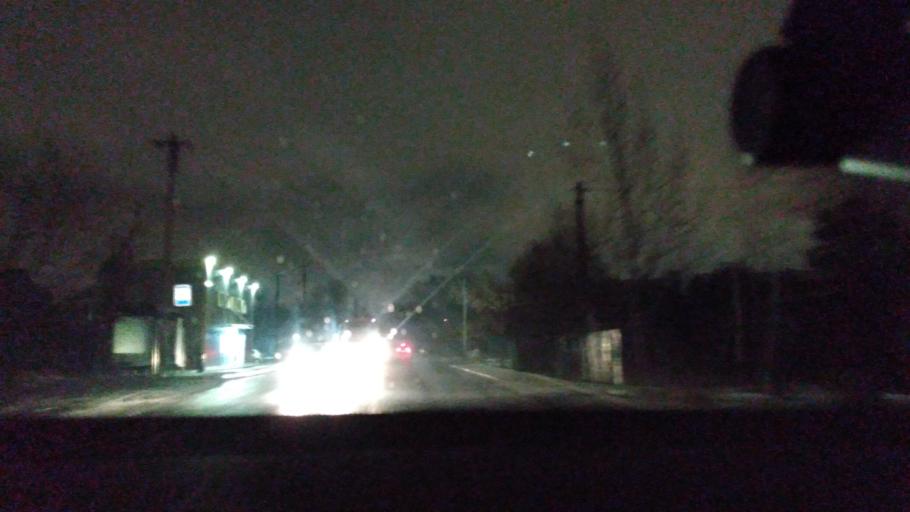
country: RU
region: Moscow
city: Khimki
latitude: 55.9262
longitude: 37.4331
